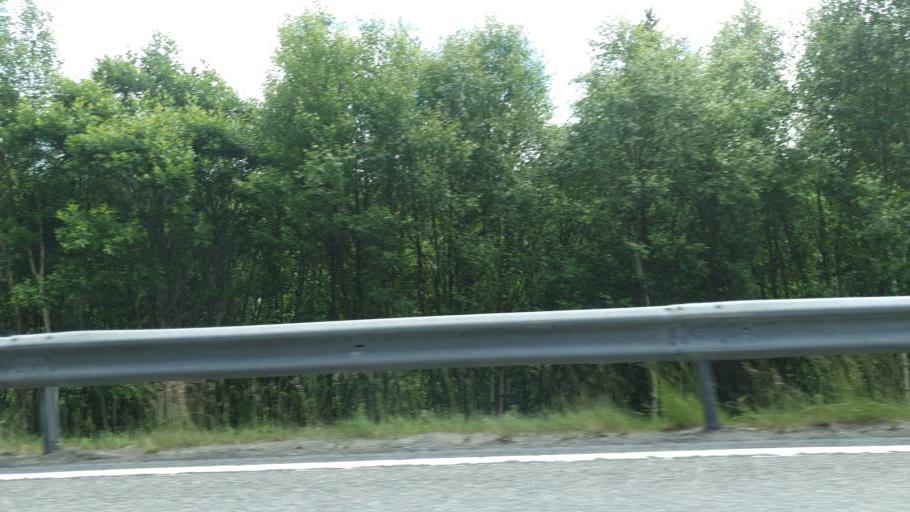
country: NO
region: Sor-Trondelag
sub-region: Rennebu
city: Berkak
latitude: 62.6684
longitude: 9.9009
